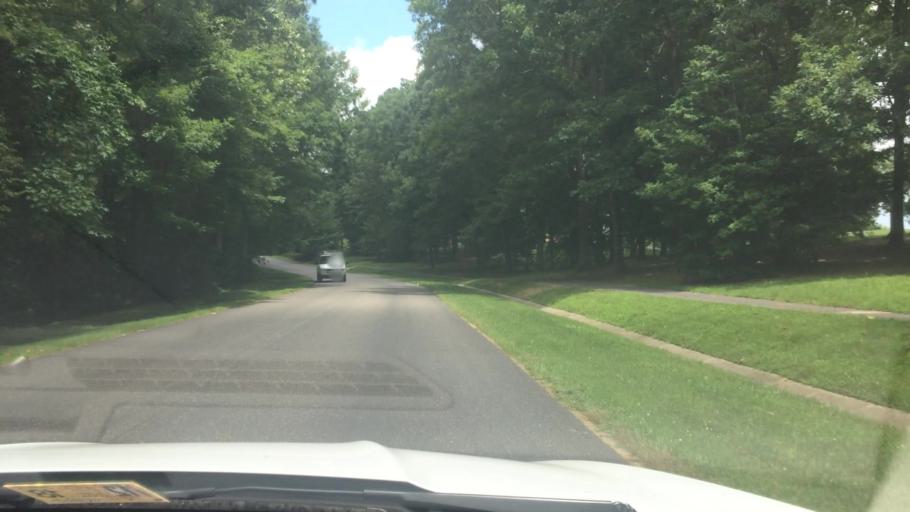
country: US
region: Virginia
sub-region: James City County
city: Williamsburg
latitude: 37.3057
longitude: -76.7953
